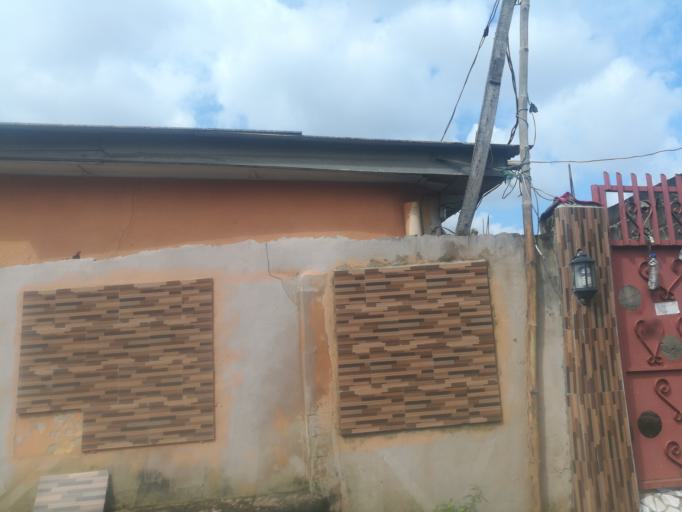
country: NG
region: Lagos
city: Somolu
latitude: 6.5493
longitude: 3.3733
